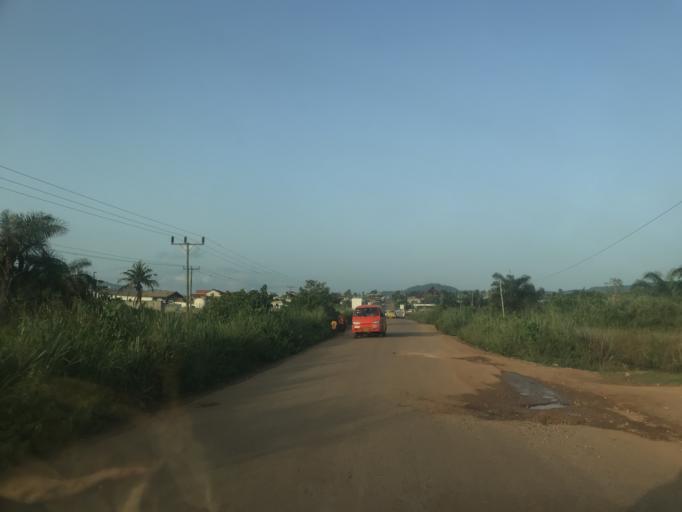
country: GH
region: Ashanti
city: Obuasi
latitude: 6.2020
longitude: -1.6130
